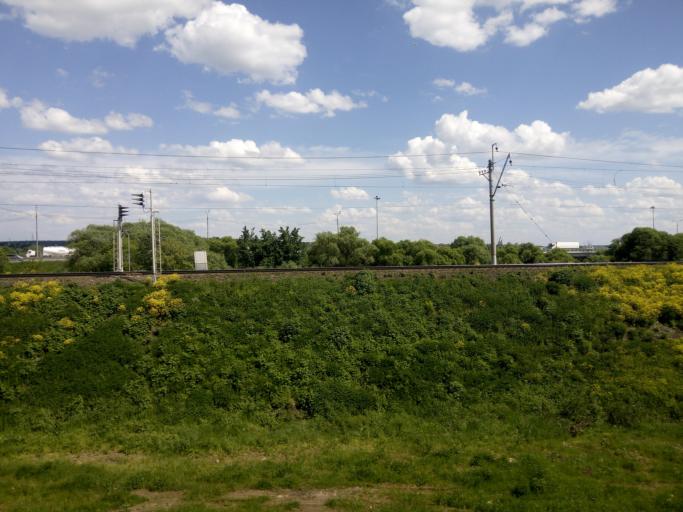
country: RU
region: Moskovskaya
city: Yam
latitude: 55.4967
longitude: 37.7281
